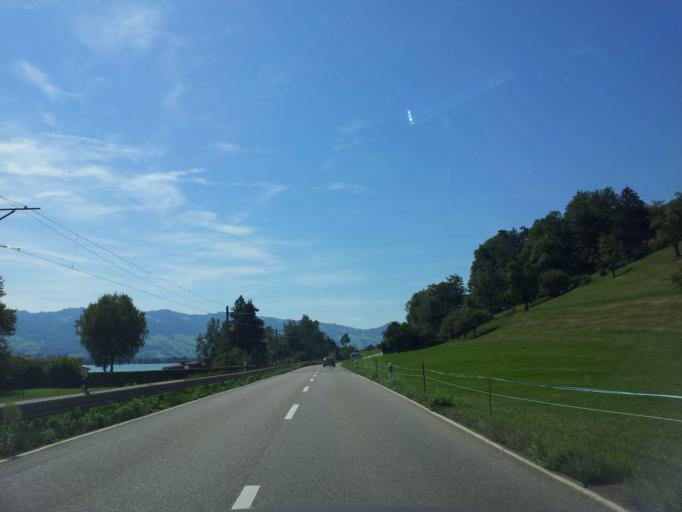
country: CH
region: Saint Gallen
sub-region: Wahlkreis See-Gaster
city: Eschenbach
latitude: 47.2238
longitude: 8.9101
